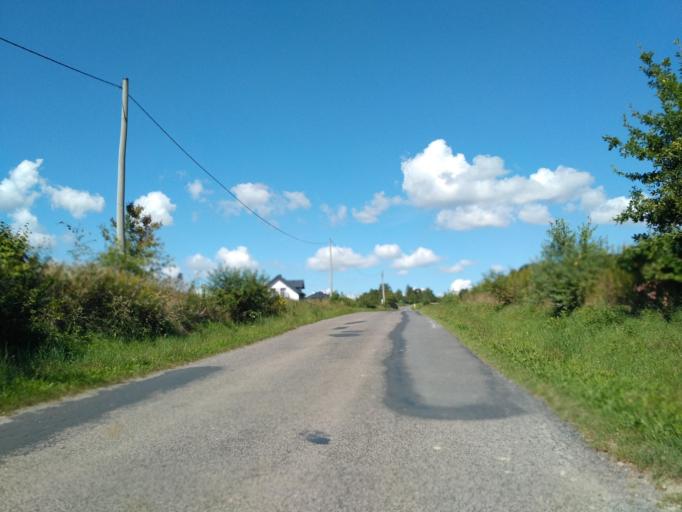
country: PL
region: Subcarpathian Voivodeship
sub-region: Powiat jasielski
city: Skolyszyn
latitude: 49.8023
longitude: 21.3142
